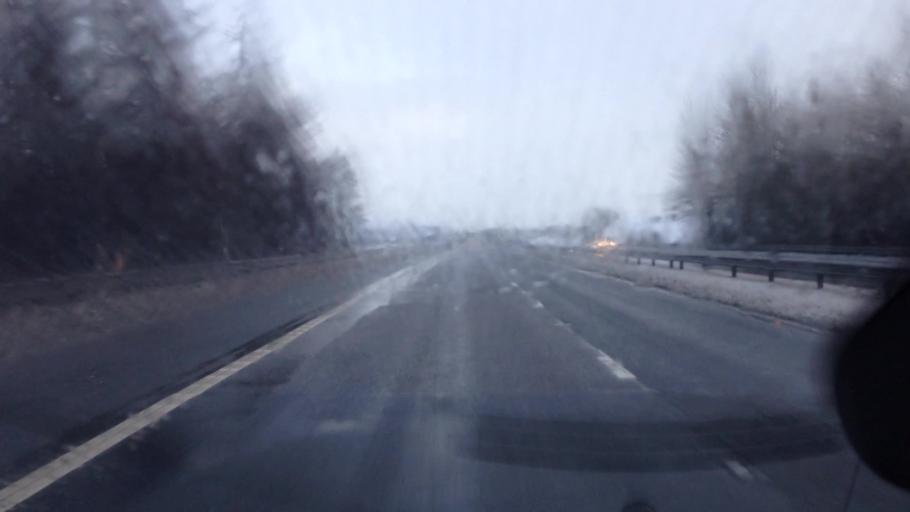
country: GB
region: Scotland
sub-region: South Lanarkshire
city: Blackwood
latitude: 55.6587
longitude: -3.9111
